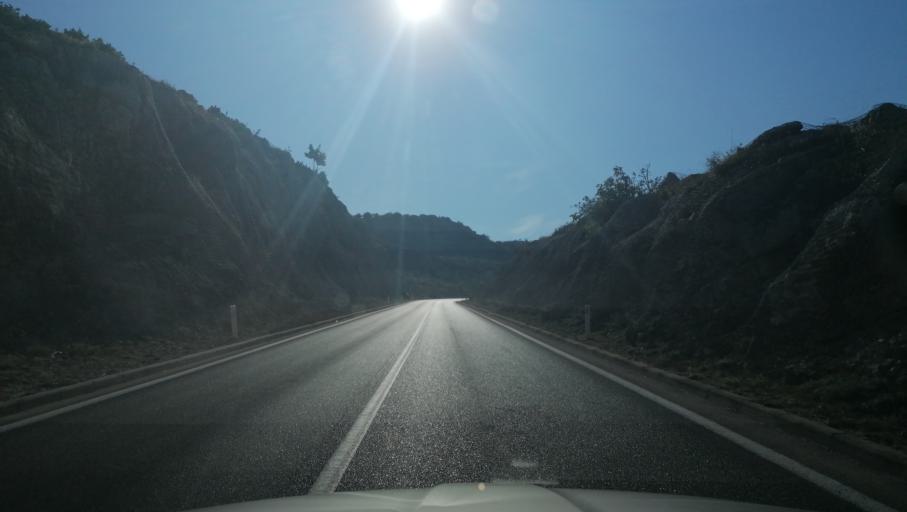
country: BA
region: Republika Srpska
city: Trebinje
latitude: 42.6750
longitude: 18.3434
